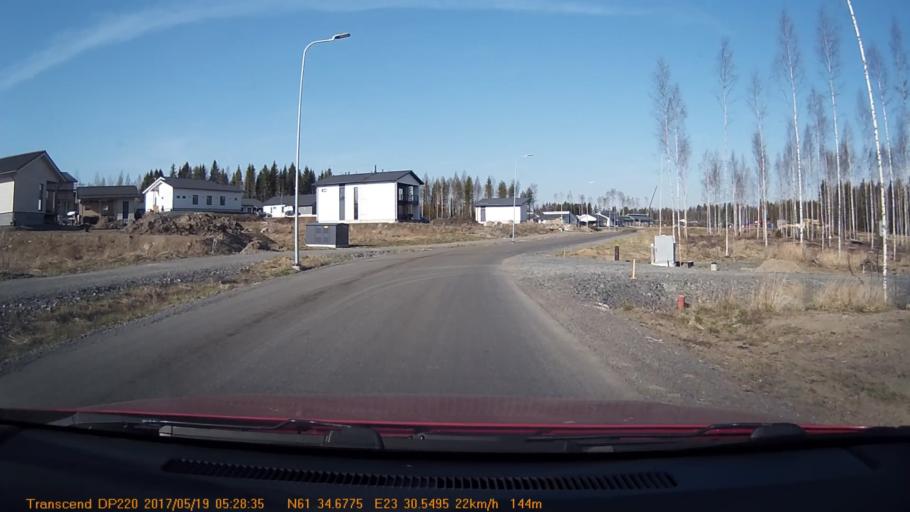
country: FI
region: Pirkanmaa
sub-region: Tampere
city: Yloejaervi
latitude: 61.5777
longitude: 23.5096
